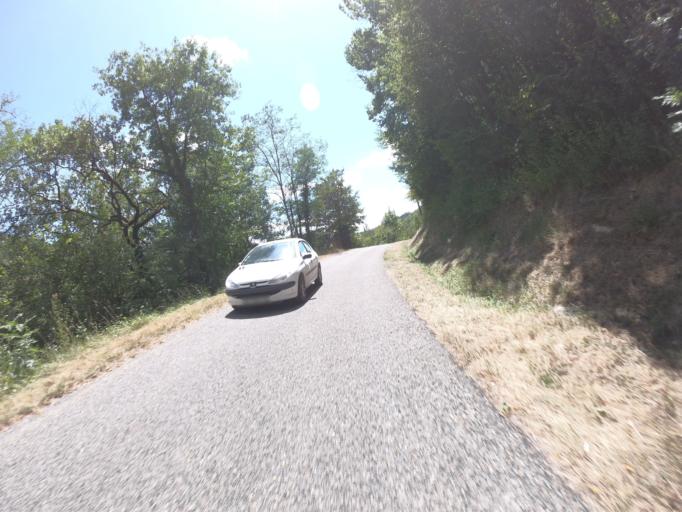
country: FR
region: Midi-Pyrenees
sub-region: Departement de l'Ariege
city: Mirepoix
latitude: 43.0725
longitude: 1.8417
